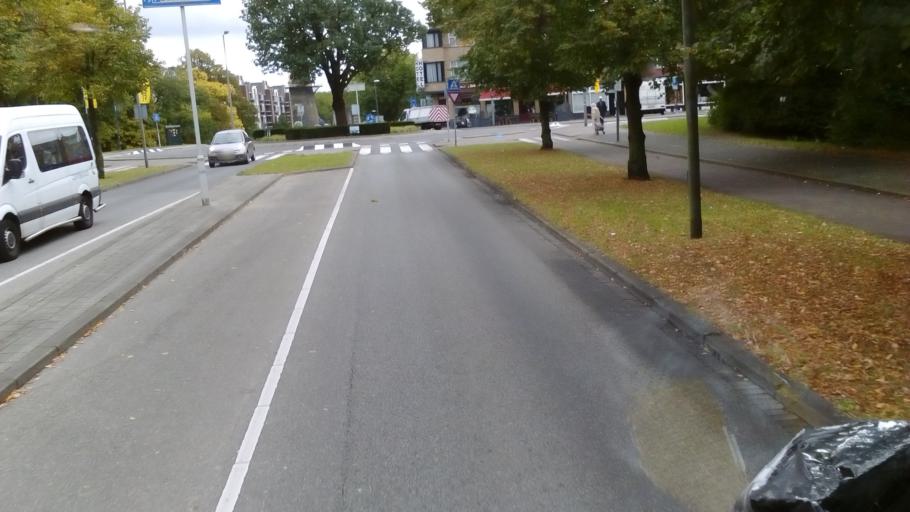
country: NL
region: South Holland
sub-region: Gemeente Schiedam
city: Schiedam
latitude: 51.9177
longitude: 4.3913
